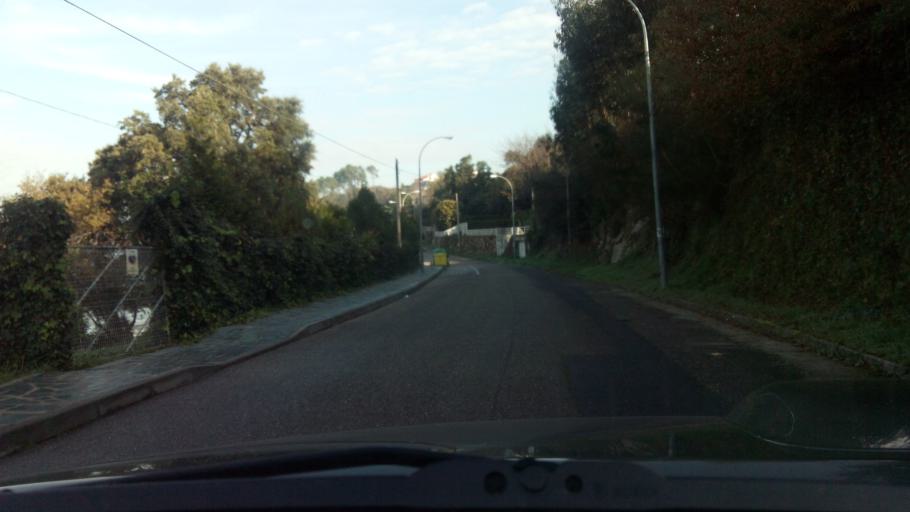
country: ES
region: Galicia
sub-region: Provincia de Pontevedra
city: Marin
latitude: 42.3749
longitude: -8.7297
